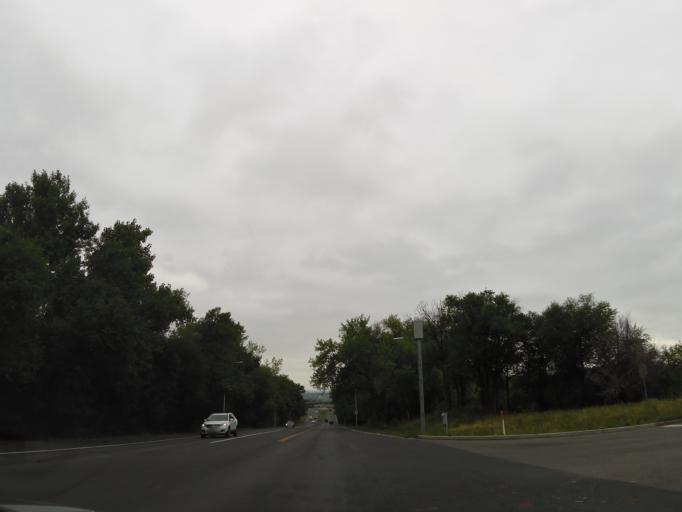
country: US
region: Colorado
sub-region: El Paso County
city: Colorado Springs
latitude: 38.7954
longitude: -104.8305
